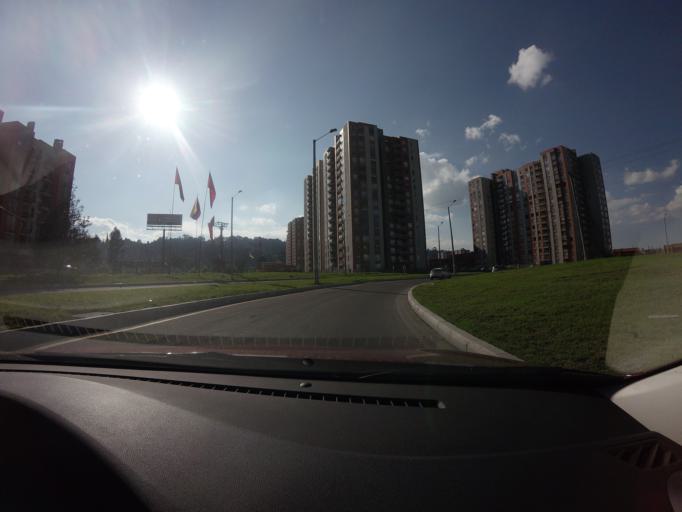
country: CO
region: Cundinamarca
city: Cota
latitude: 4.7430
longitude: -74.0660
